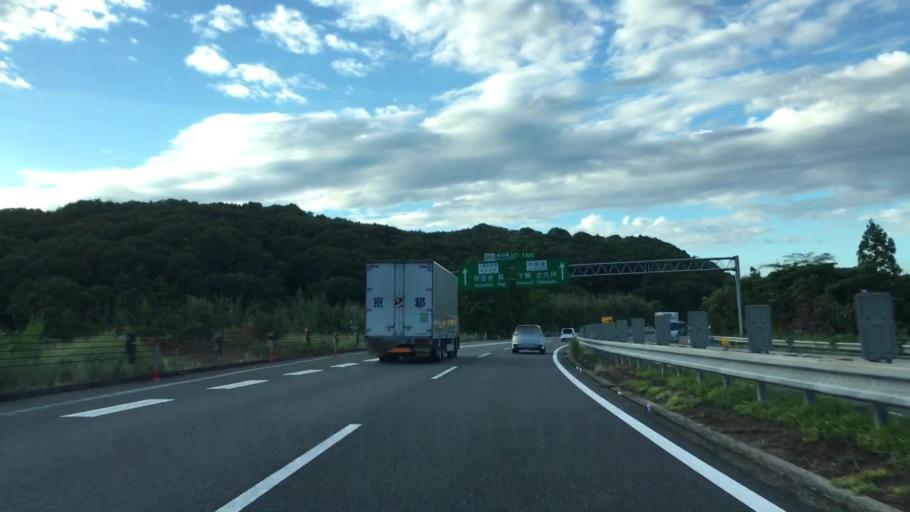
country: JP
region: Yamaguchi
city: Ogori-shimogo
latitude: 34.1641
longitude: 131.3264
